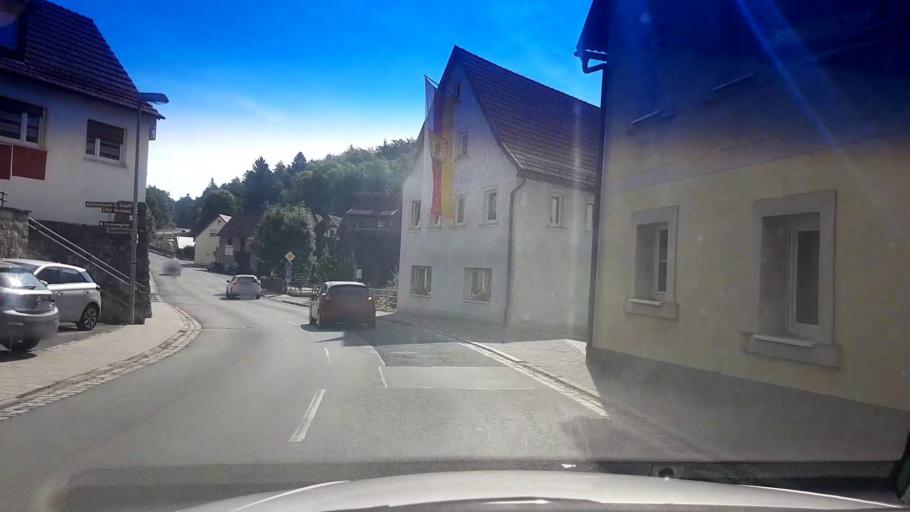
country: DE
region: Bavaria
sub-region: Upper Franconia
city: Hollfeld
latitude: 49.9378
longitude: 11.2939
